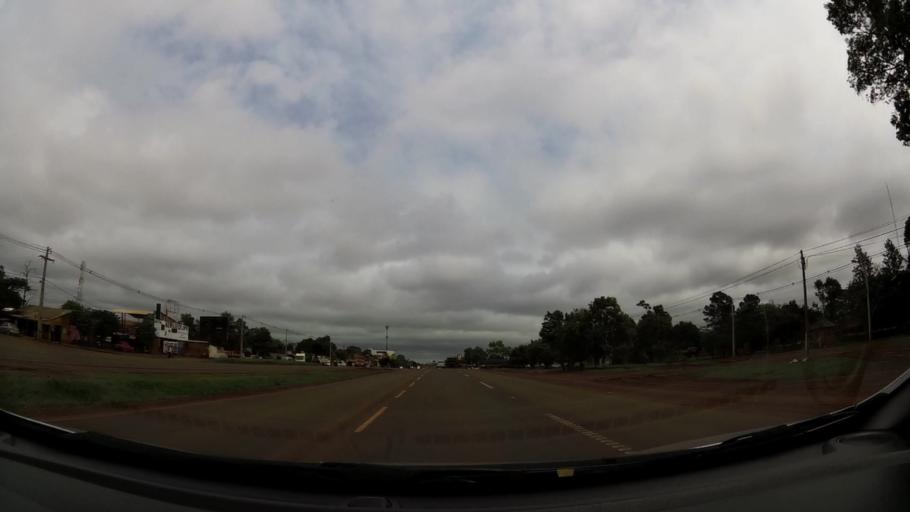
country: PY
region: Alto Parana
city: Ciudad del Este
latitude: -25.4924
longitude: -54.7319
